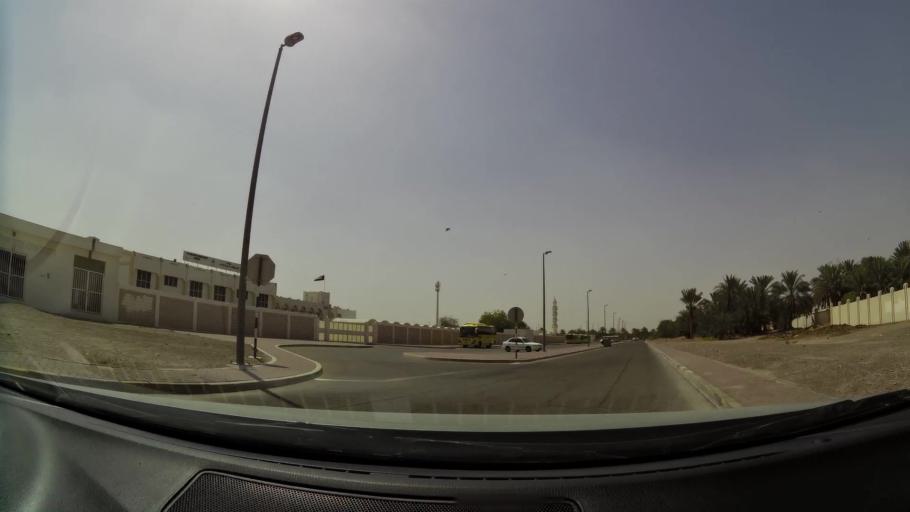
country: AE
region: Abu Dhabi
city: Al Ain
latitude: 24.2298
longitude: 55.7055
